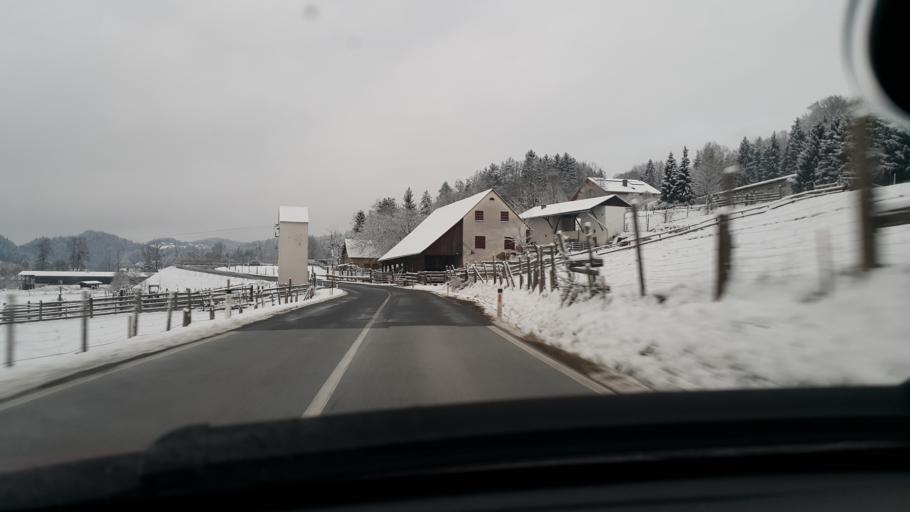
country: AT
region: Styria
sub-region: Politischer Bezirk Graz-Umgebung
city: Sankt Oswald bei Plankenwarth
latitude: 47.0736
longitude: 15.2668
